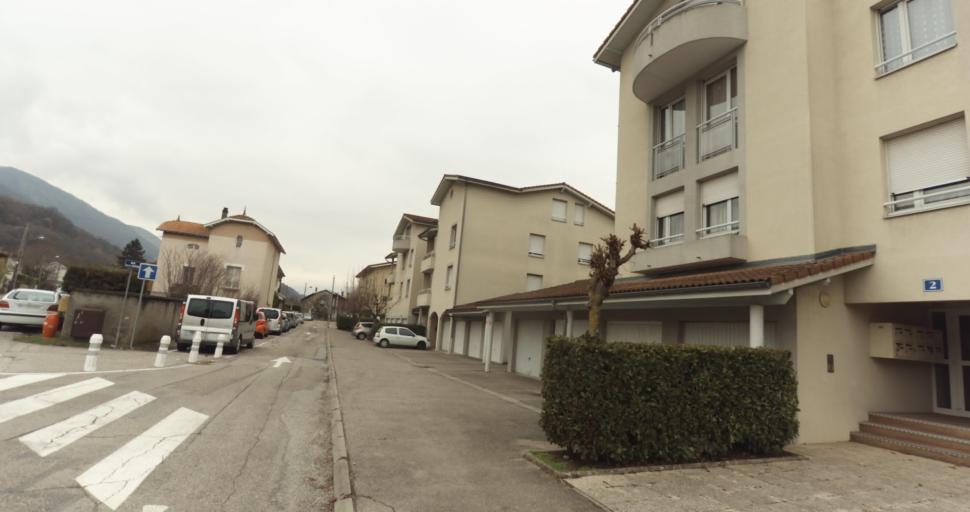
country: FR
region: Rhone-Alpes
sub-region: Departement de l'Isere
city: Vif
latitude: 45.0518
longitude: 5.6684
